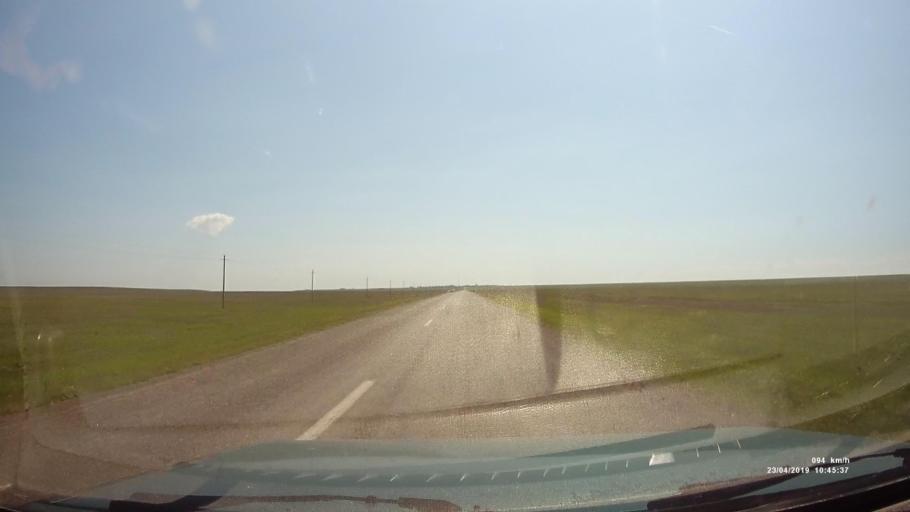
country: RU
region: Kalmykiya
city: Yashalta
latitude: 46.4499
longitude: 42.6775
